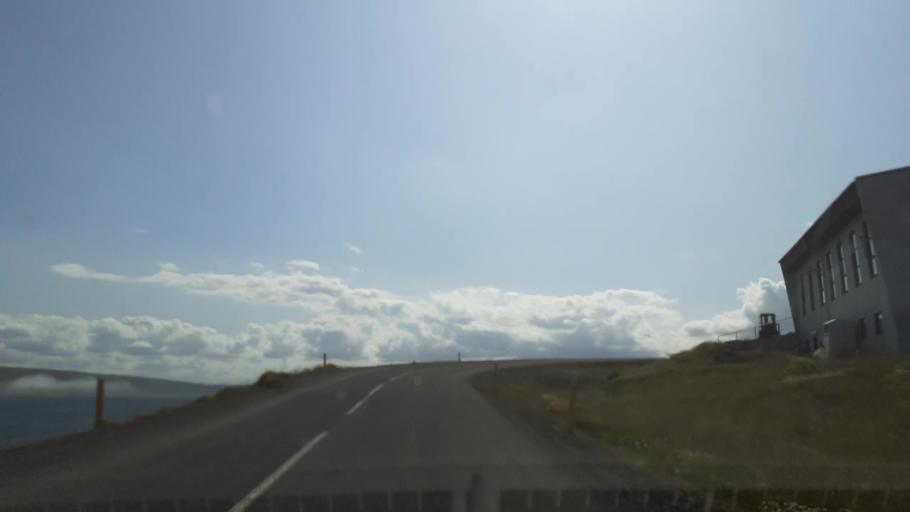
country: IS
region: West
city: Borgarnes
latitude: 65.2077
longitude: -21.0973
